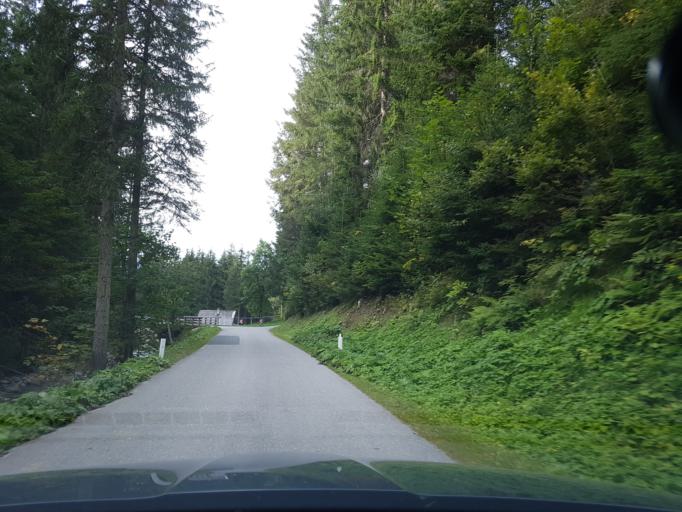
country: AT
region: Salzburg
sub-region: Politischer Bezirk Sankt Johann im Pongau
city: Forstau
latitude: 47.3555
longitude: 13.5694
